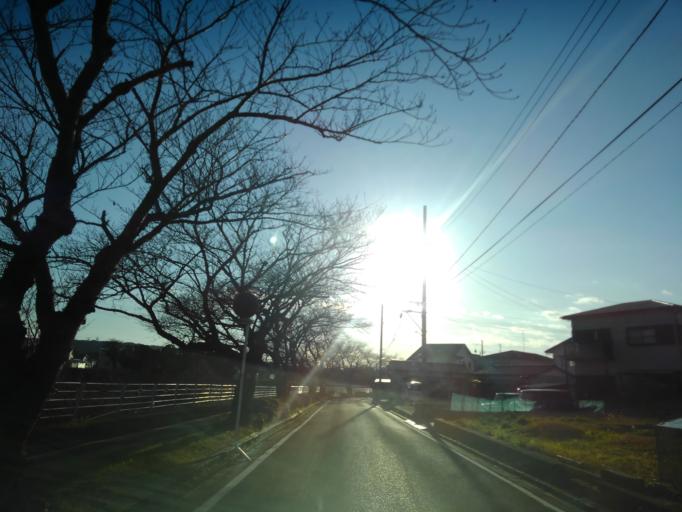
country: JP
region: Chiba
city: Kimitsu
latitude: 35.3242
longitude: 139.9025
